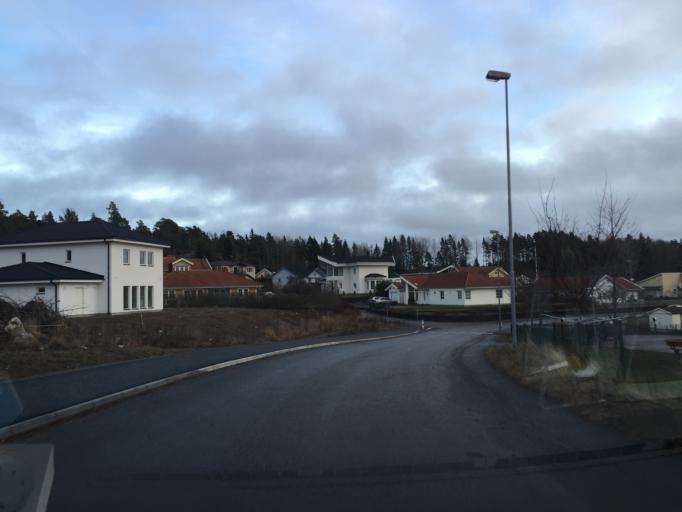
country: SE
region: Stockholm
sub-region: Sodertalje Kommun
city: Soedertaelje
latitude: 59.2234
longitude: 17.6400
